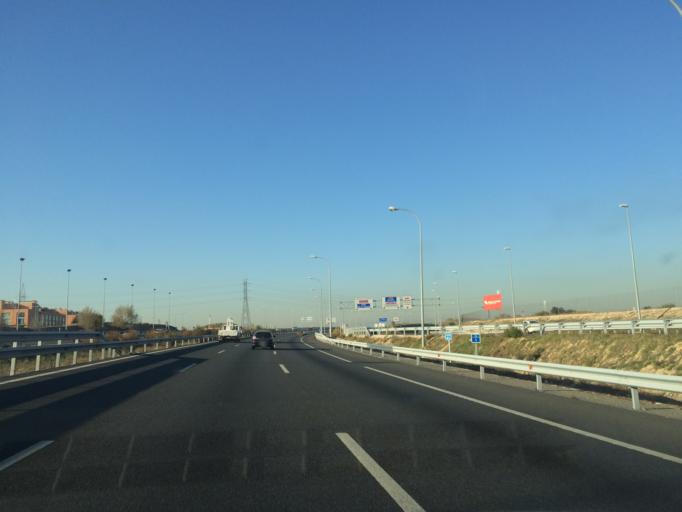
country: ES
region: Madrid
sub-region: Provincia de Madrid
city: Pozuelo de Alarcon
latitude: 40.3923
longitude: -3.8312
